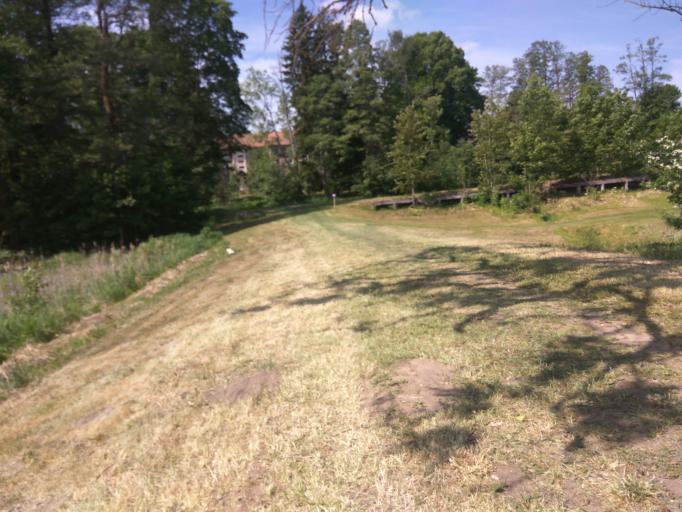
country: LV
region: Kuldigas Rajons
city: Kuldiga
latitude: 56.9210
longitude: 21.9715
